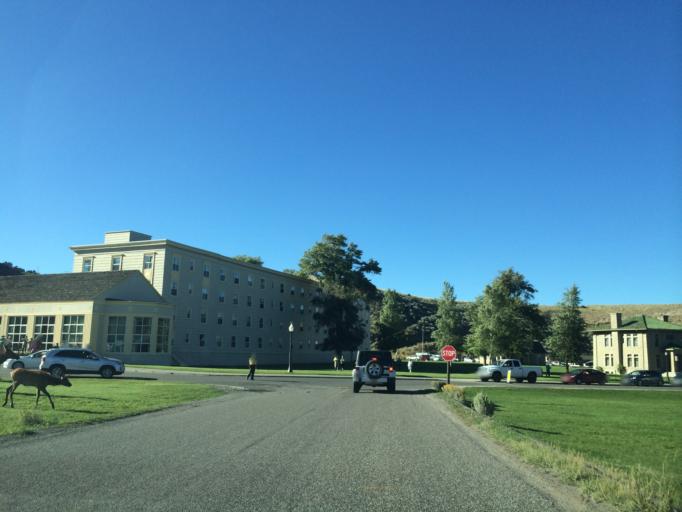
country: US
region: Montana
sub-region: Gallatin County
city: West Yellowstone
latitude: 44.9760
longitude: -110.7007
